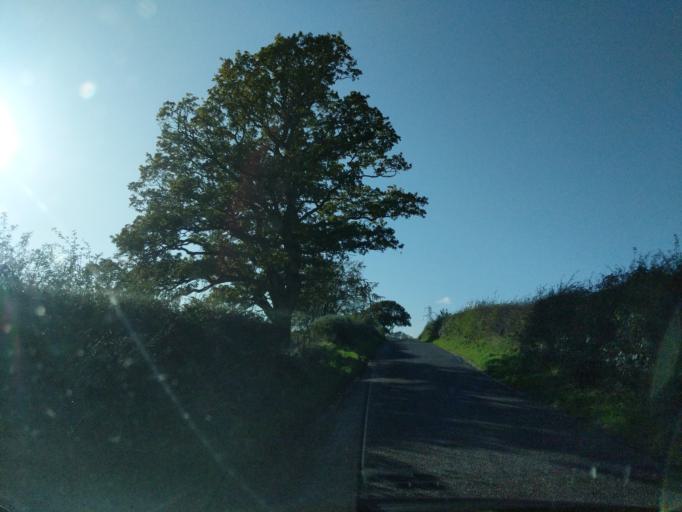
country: GB
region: Scotland
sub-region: Dumfries and Galloway
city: Dumfries
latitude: 55.0430
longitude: -3.7378
